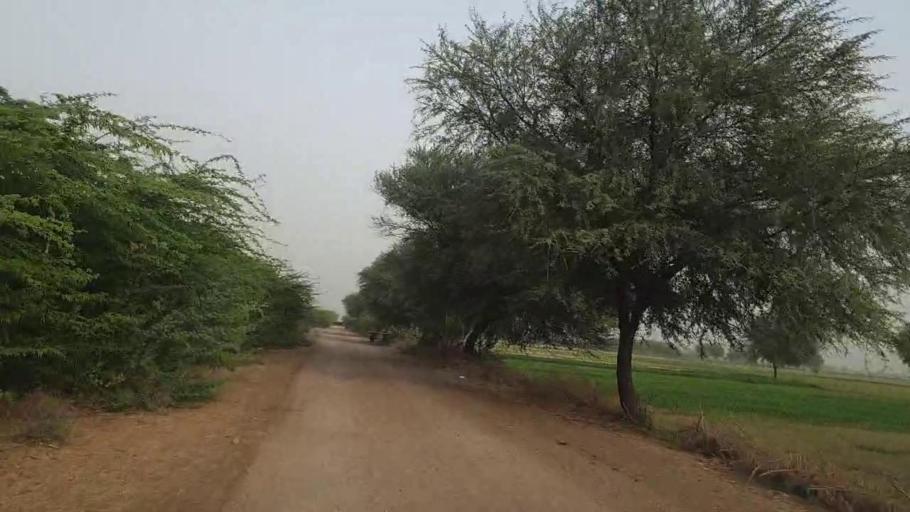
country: PK
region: Sindh
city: Kunri
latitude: 25.0968
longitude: 69.4440
